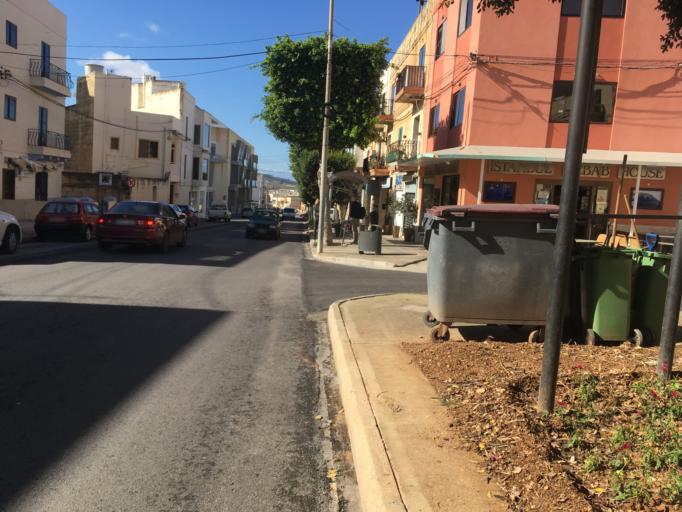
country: MT
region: In-Naxxar
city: Naxxar
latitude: 35.9134
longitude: 14.4389
